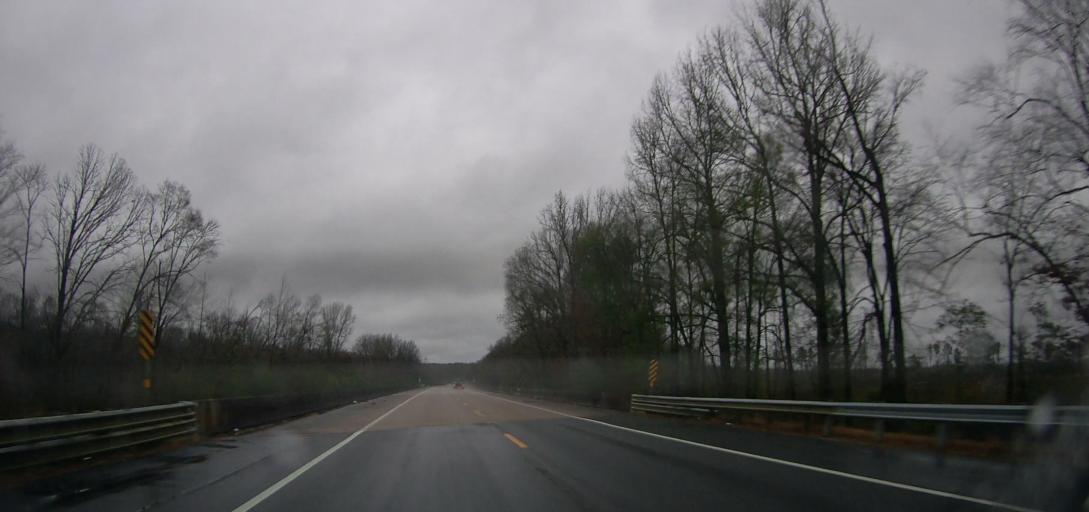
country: US
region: Alabama
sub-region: Chilton County
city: Thorsby
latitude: 32.7575
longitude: -86.8724
